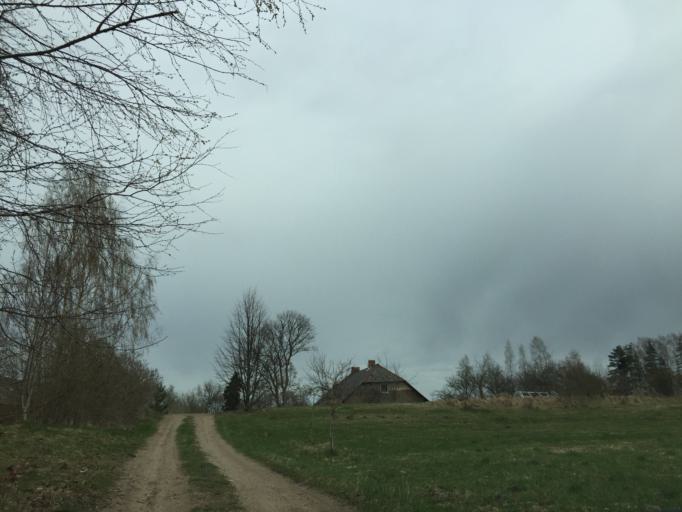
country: LV
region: Priekuli
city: Priekuli
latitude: 57.2922
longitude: 25.3292
